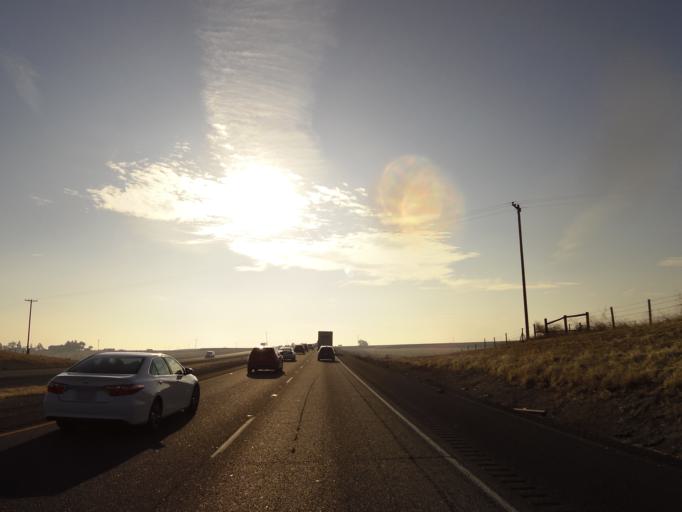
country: US
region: California
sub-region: Merced County
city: Los Banos
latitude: 37.0717
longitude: -120.9845
